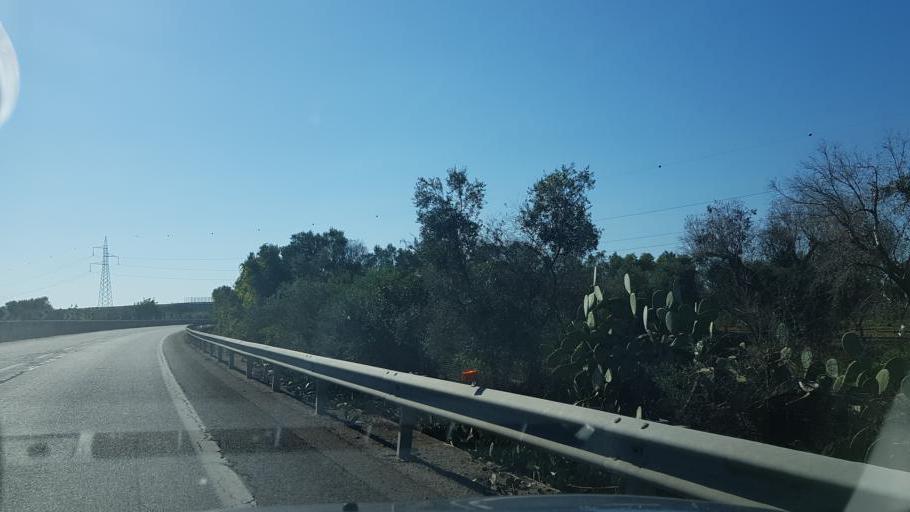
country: IT
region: Apulia
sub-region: Provincia di Brindisi
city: San Pietro Vernotico
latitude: 40.5134
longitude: 18.0226
